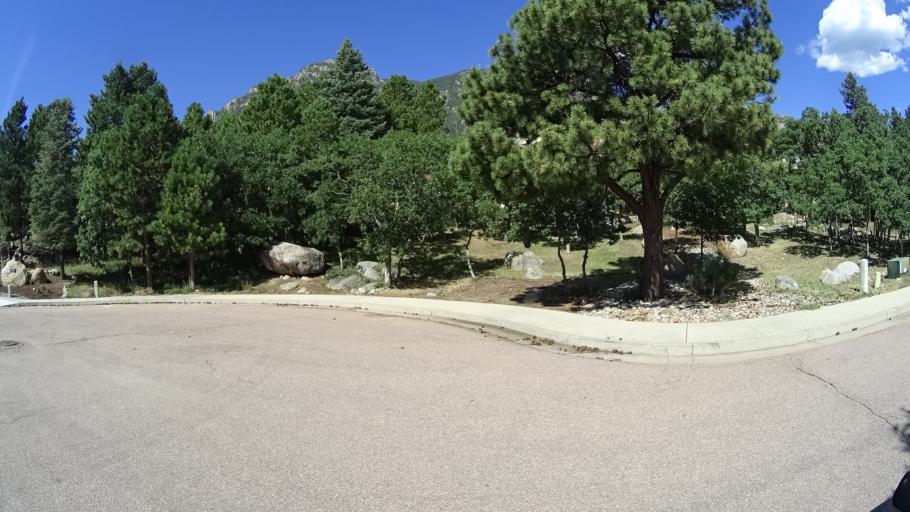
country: US
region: Colorado
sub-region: El Paso County
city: Fort Carson
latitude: 38.7460
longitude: -104.8373
